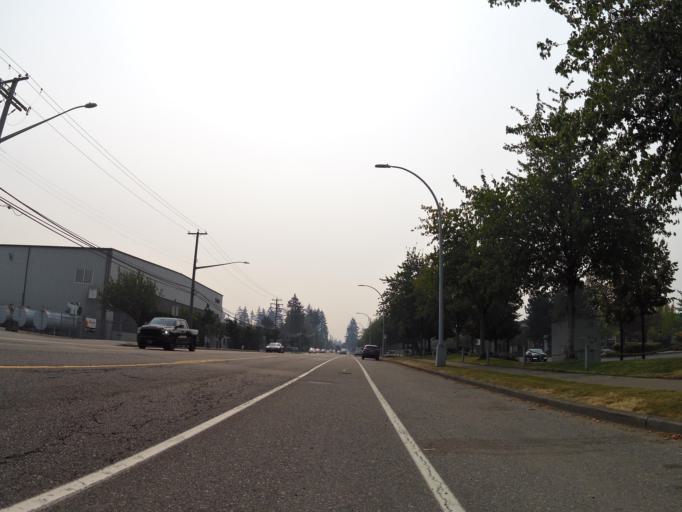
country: CA
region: British Columbia
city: Surrey
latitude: 49.1392
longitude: -122.8568
